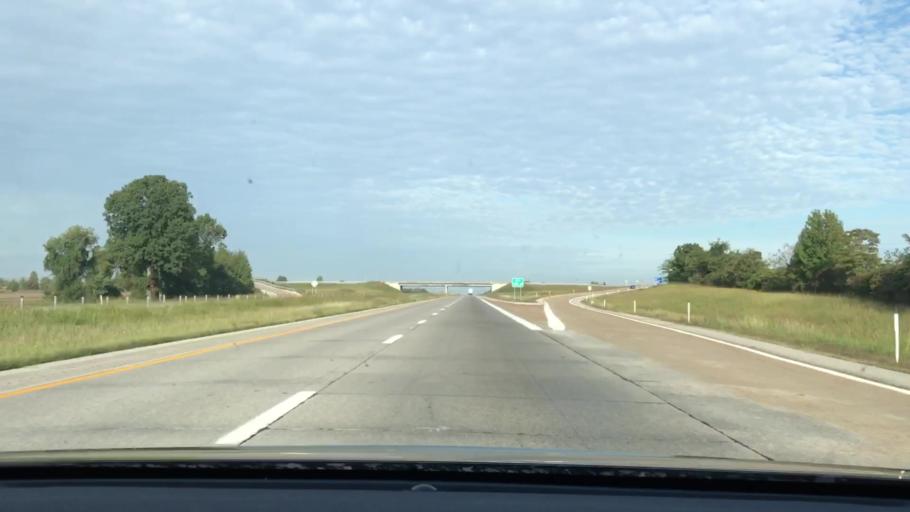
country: US
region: Kentucky
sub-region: Trigg County
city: Cadiz
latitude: 36.9649
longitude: -87.8693
